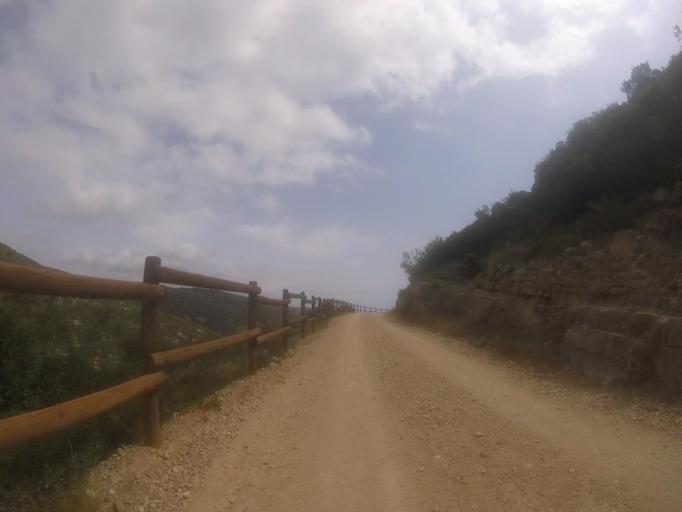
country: ES
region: Valencia
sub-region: Provincia de Castello
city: Peniscola
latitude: 40.3454
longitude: 0.3585
